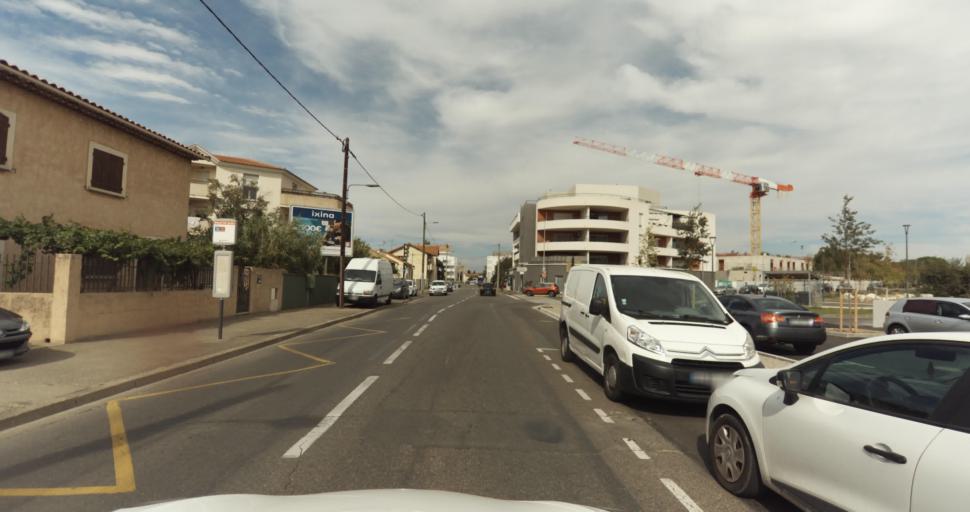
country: FR
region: Provence-Alpes-Cote d'Azur
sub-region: Departement des Bouches-du-Rhone
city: Miramas
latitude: 43.5770
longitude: 5.0007
